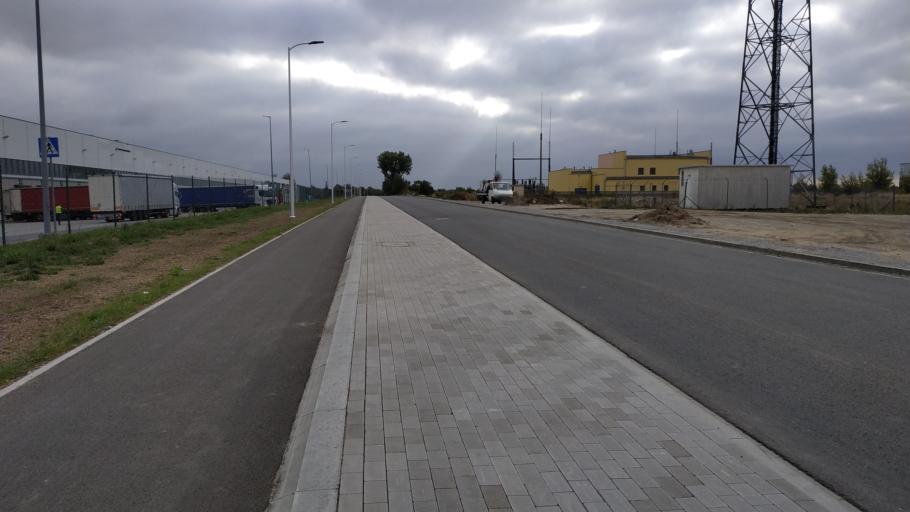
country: PL
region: Lower Silesian Voivodeship
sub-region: Powiat wroclawski
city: Bielany Wroclawskie
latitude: 51.0410
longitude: 16.9551
